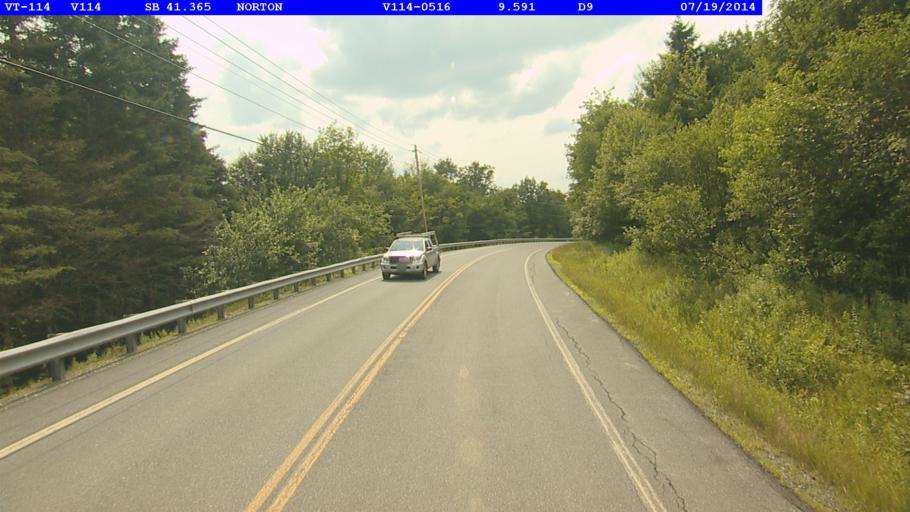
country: CA
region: Quebec
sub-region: Estrie
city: Coaticook
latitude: 44.9957
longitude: -71.7140
